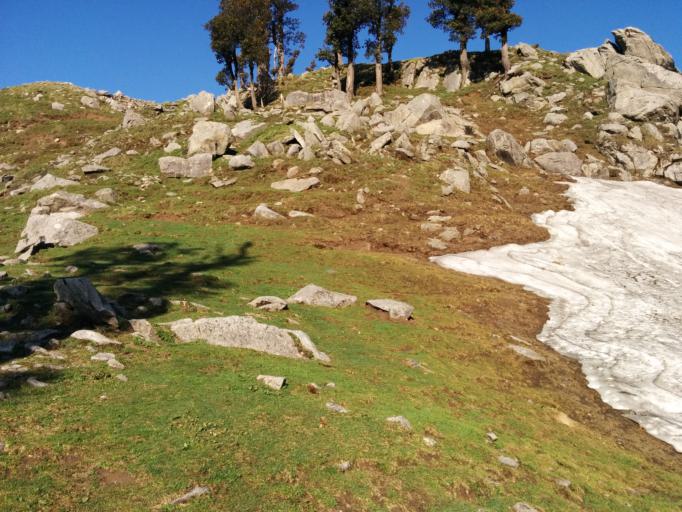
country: IN
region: Himachal Pradesh
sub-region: Kangra
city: Dharmsala
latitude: 32.2739
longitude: 76.3616
